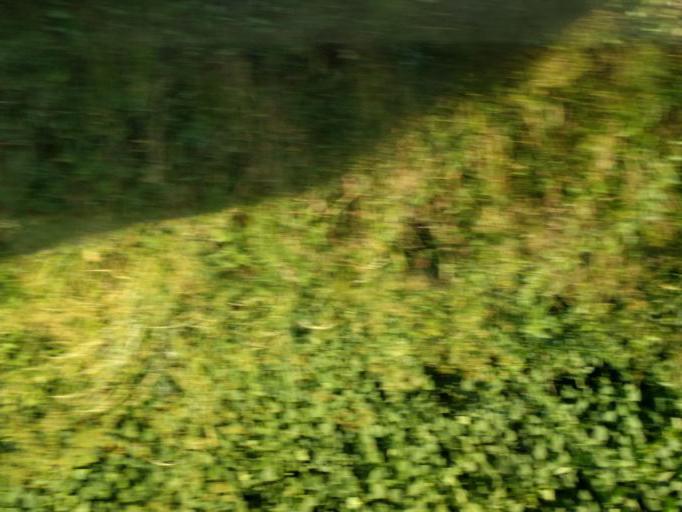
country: DK
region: South Denmark
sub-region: Kerteminde Kommune
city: Kerteminde
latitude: 55.5735
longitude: 10.6453
